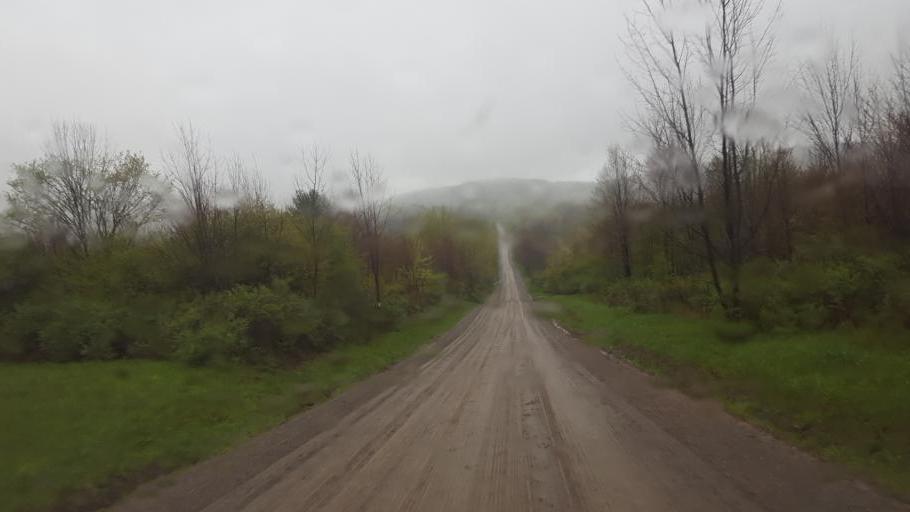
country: US
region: Pennsylvania
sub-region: Tioga County
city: Westfield
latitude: 42.0477
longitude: -77.4772
